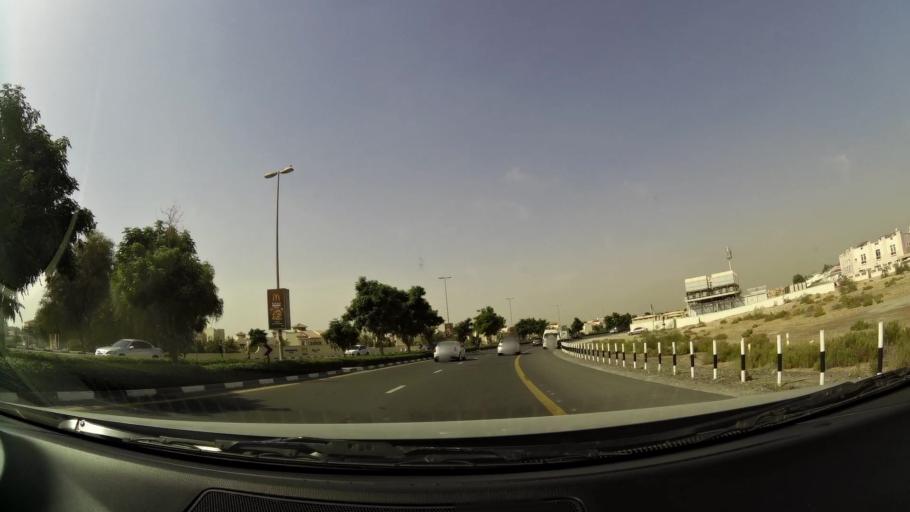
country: AE
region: Ash Shariqah
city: Sharjah
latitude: 25.2157
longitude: 55.4270
